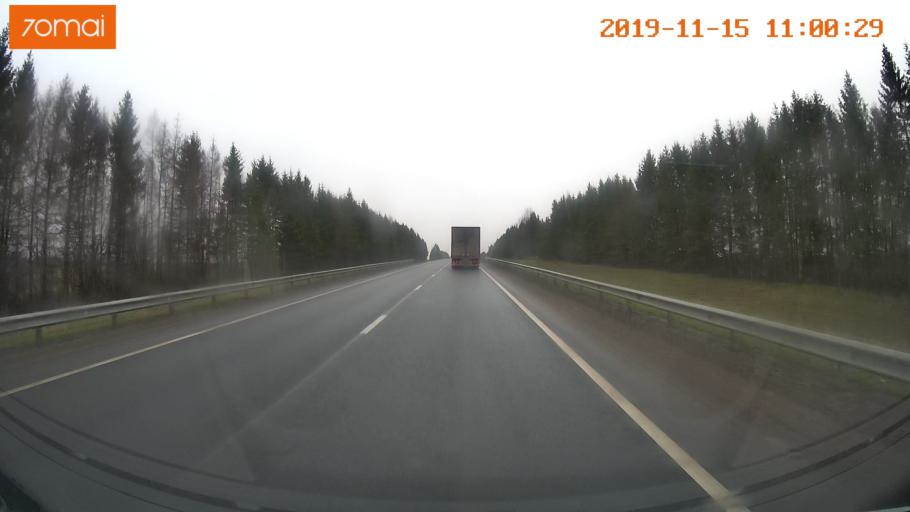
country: RU
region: Vologda
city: Chebsara
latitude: 59.1369
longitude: 38.9005
